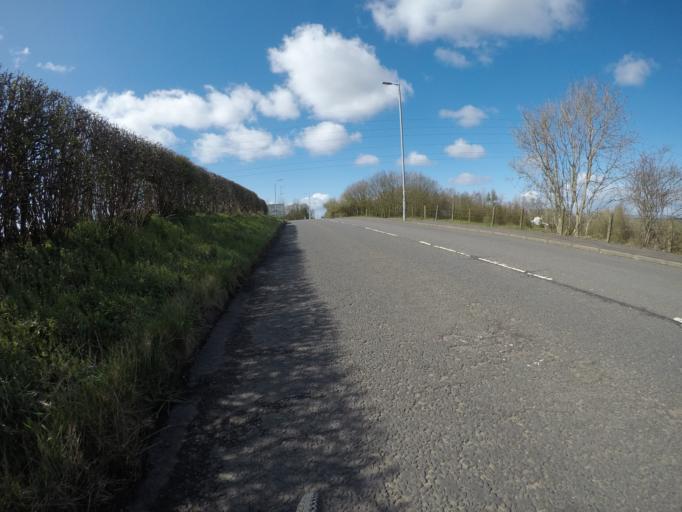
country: GB
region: Scotland
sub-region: North Ayrshire
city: Springside
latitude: 55.6127
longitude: -4.6016
